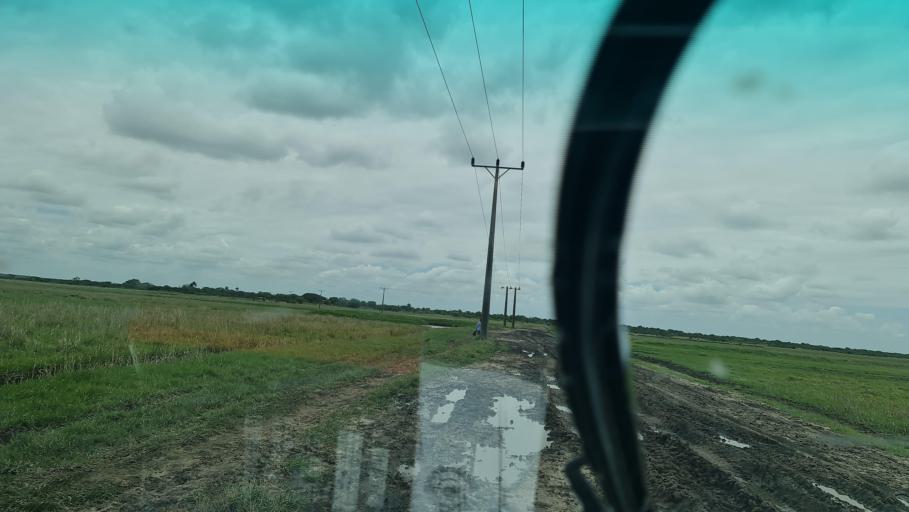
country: MZ
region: Maputo City
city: Maputo
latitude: -25.7085
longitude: 32.7033
